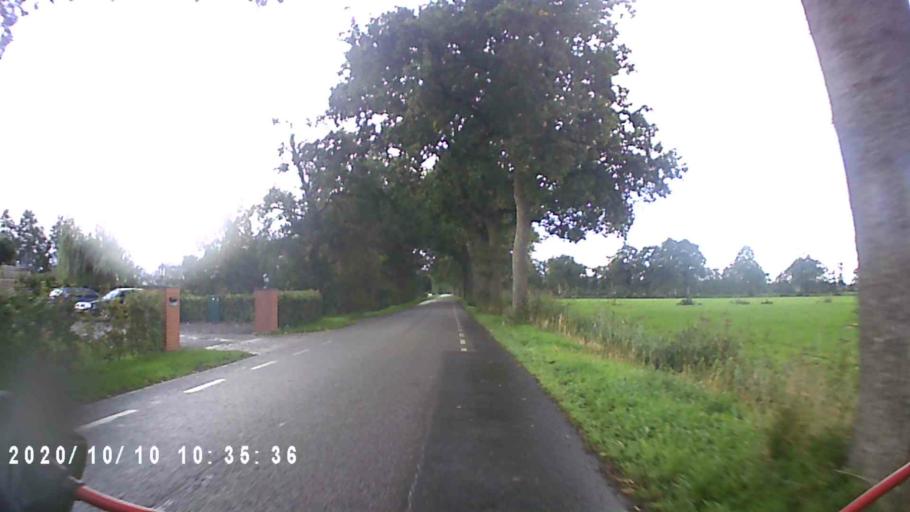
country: NL
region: Groningen
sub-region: Gemeente Grootegast
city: Grootegast
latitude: 53.1891
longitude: 6.3081
